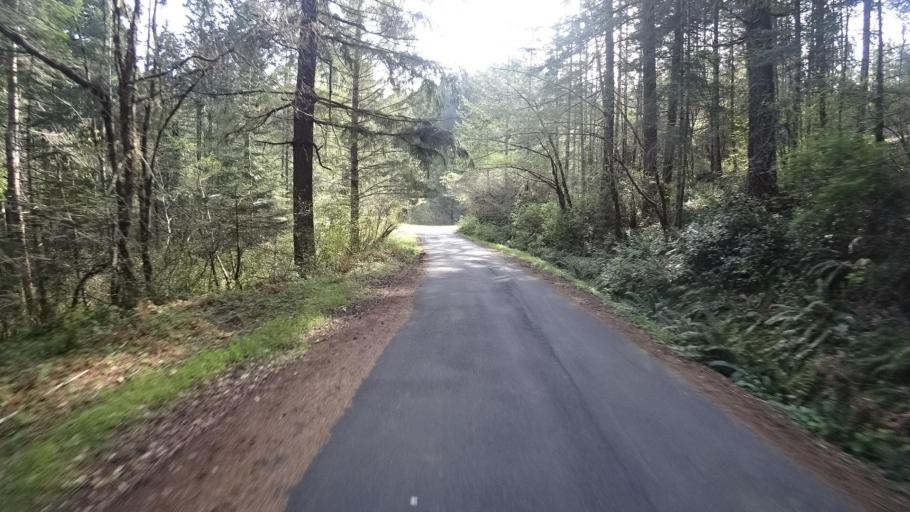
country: US
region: California
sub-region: Humboldt County
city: Blue Lake
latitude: 40.6965
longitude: -123.9383
